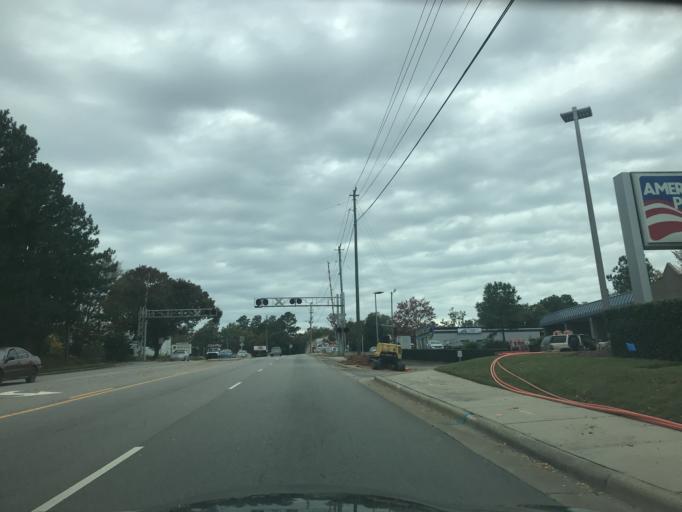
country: US
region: North Carolina
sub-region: Wake County
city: Raleigh
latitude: 35.8496
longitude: -78.6029
